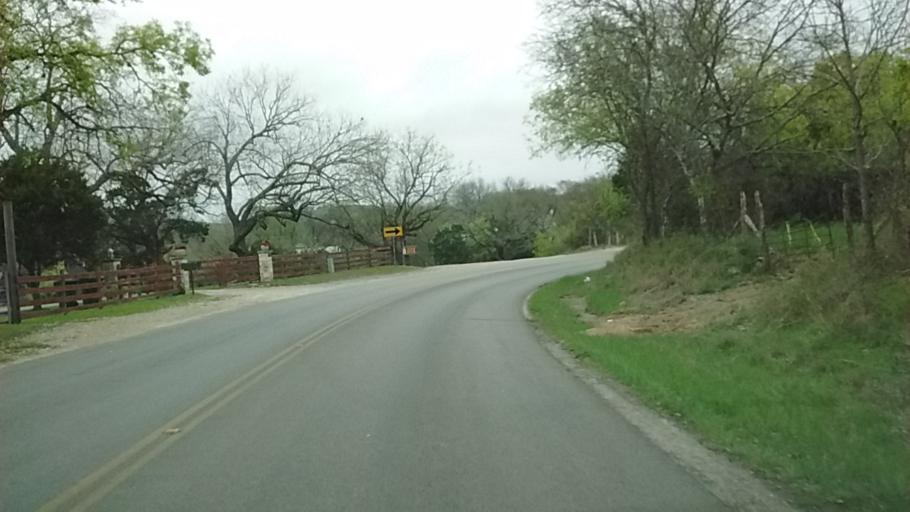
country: US
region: Texas
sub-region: Comal County
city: Canyon Lake
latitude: 29.8409
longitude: -98.1685
